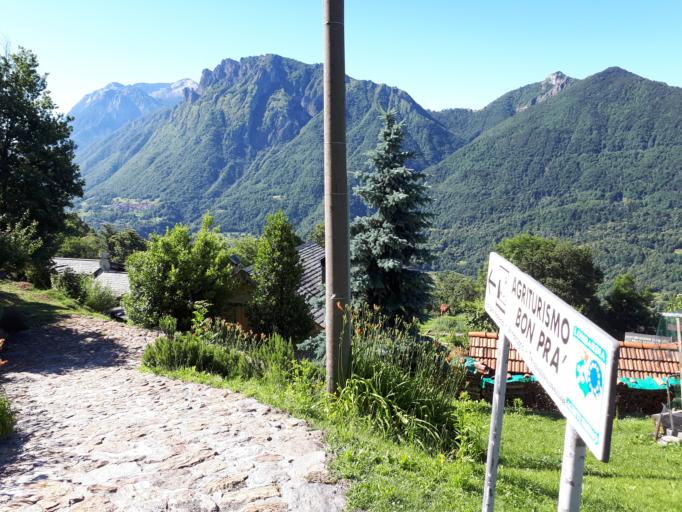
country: IT
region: Lombardy
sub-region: Provincia di Lecco
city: Vendrogno
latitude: 46.0387
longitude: 9.3261
